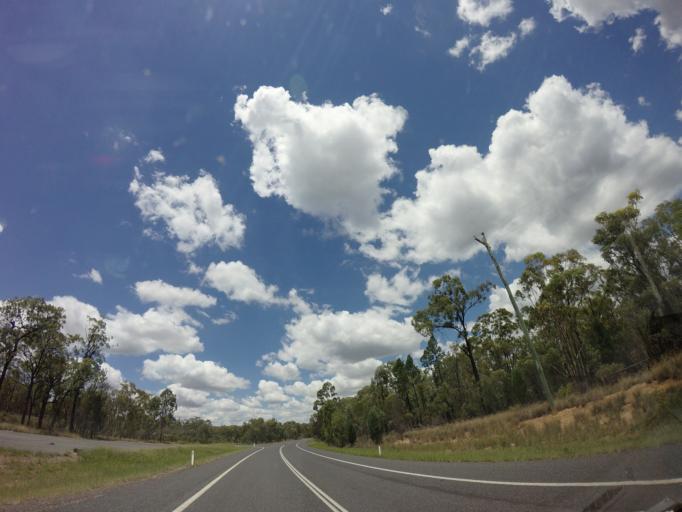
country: AU
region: Queensland
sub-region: Western Downs
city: Dalby
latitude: -27.9667
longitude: 151.0055
